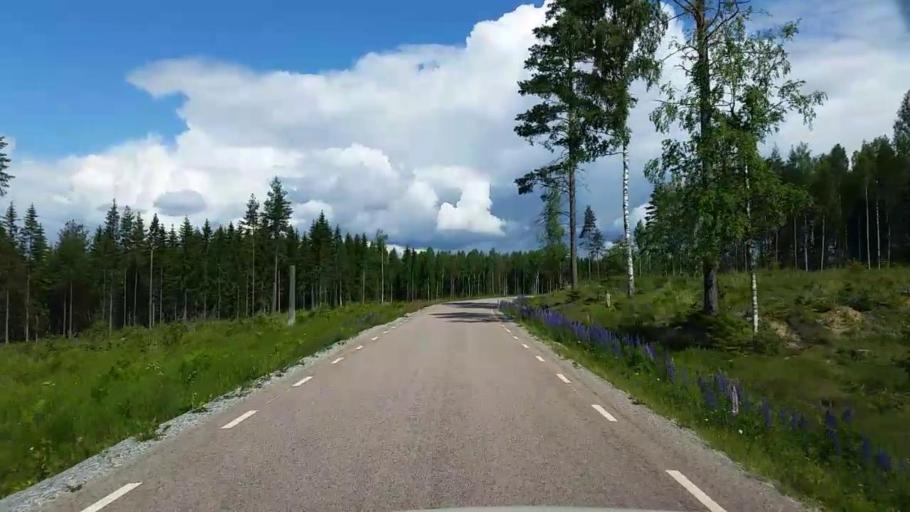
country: SE
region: Vaestmanland
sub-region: Fagersta Kommun
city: Fagersta
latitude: 59.9898
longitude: 15.7413
